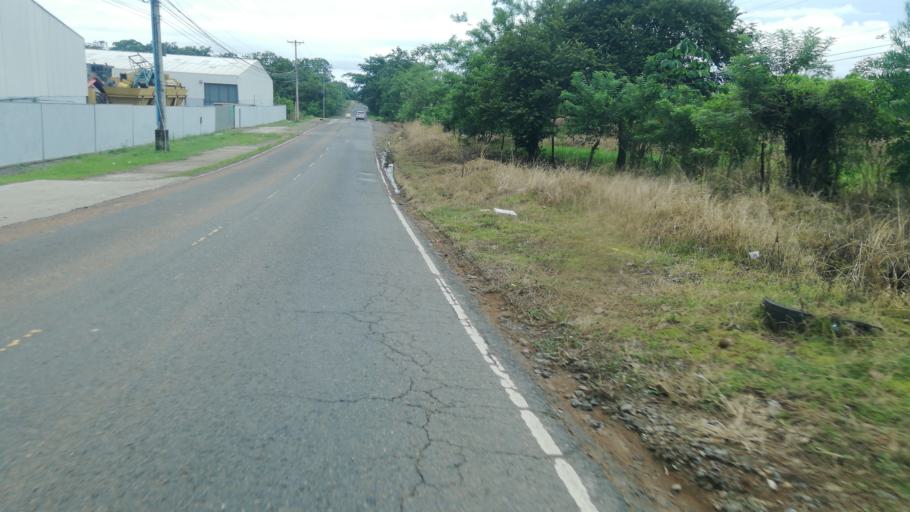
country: PA
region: Panama
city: Pacora
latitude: 9.0956
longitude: -79.2885
